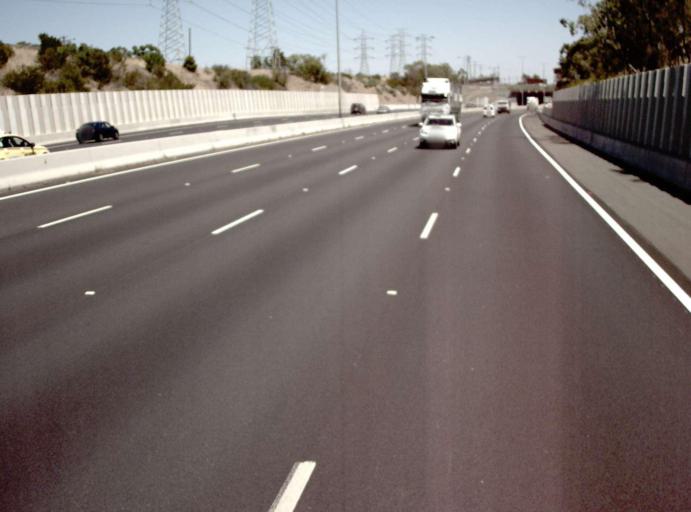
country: AU
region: Victoria
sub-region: Hume
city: Jacana
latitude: -37.6944
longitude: 144.9206
